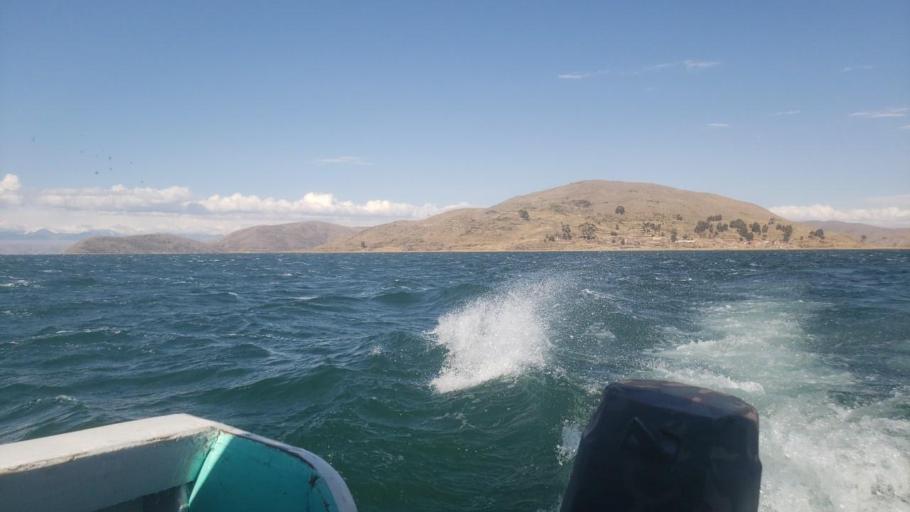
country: BO
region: La Paz
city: Huatajata
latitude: -16.3236
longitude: -68.7294
